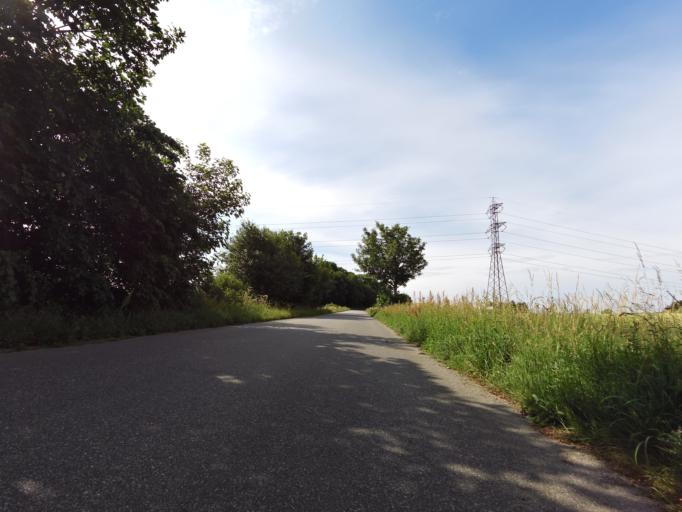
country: DK
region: Central Jutland
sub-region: Arhus Kommune
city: Kolt
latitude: 56.1256
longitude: 10.0802
